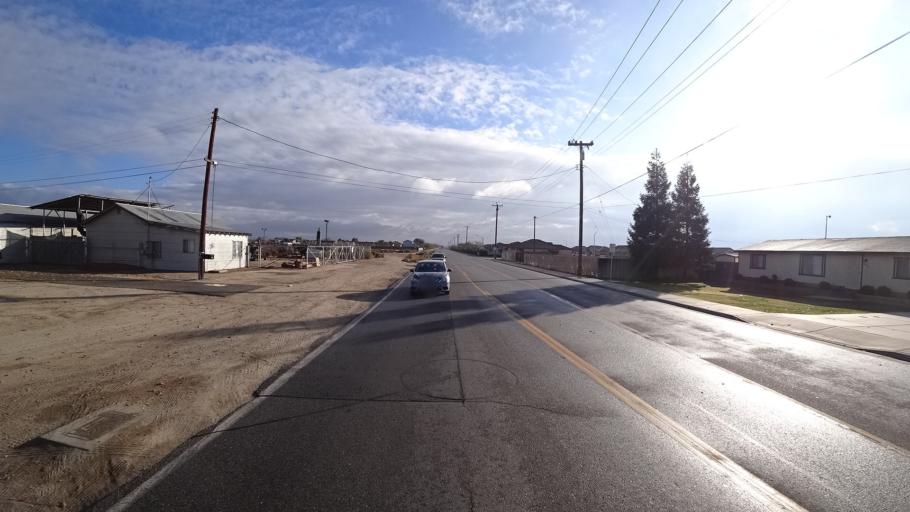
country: US
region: California
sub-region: Kern County
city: Greenfield
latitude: 35.2886
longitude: -119.0019
